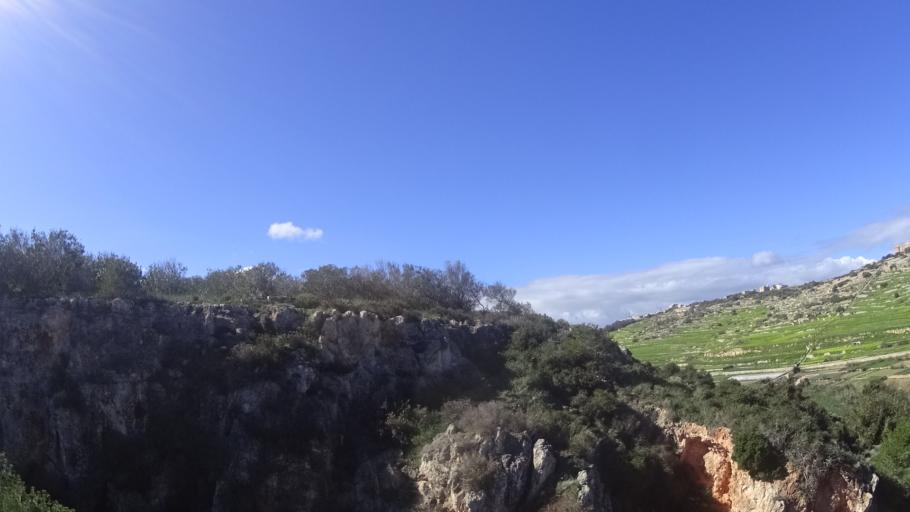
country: MT
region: Saint Paul's Bay
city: San Pawl il-Bahar
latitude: 35.9566
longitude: 14.3900
